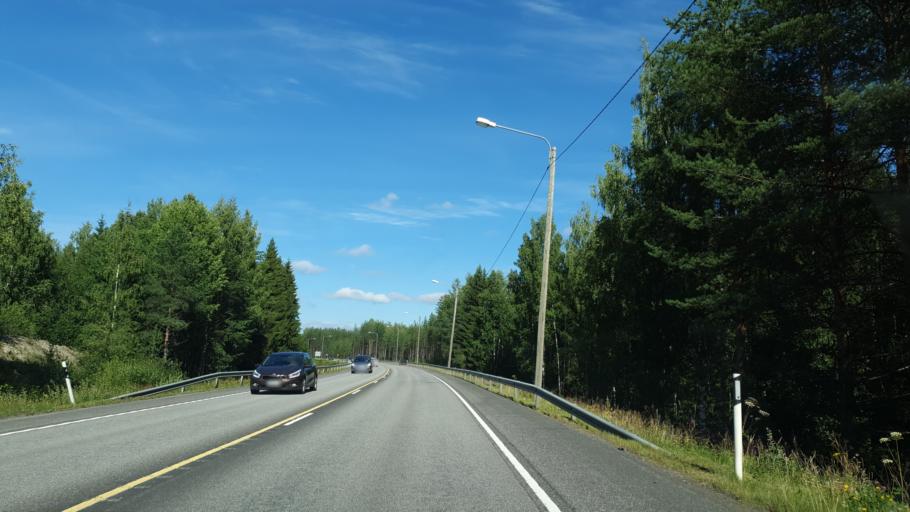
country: FI
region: Central Finland
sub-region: Jyvaeskylae
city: Toivakka
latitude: 62.2385
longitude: 25.9777
